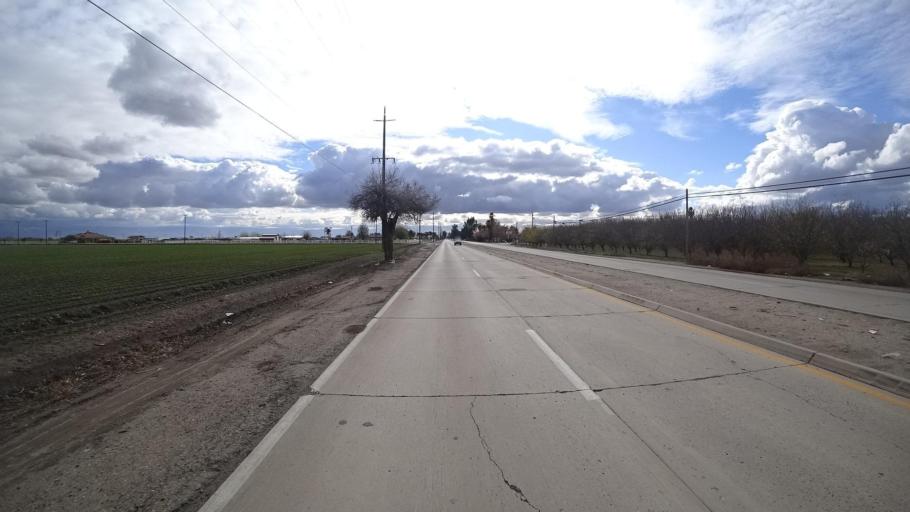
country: US
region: California
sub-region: Kern County
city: Greenfield
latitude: 35.2606
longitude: -119.0030
